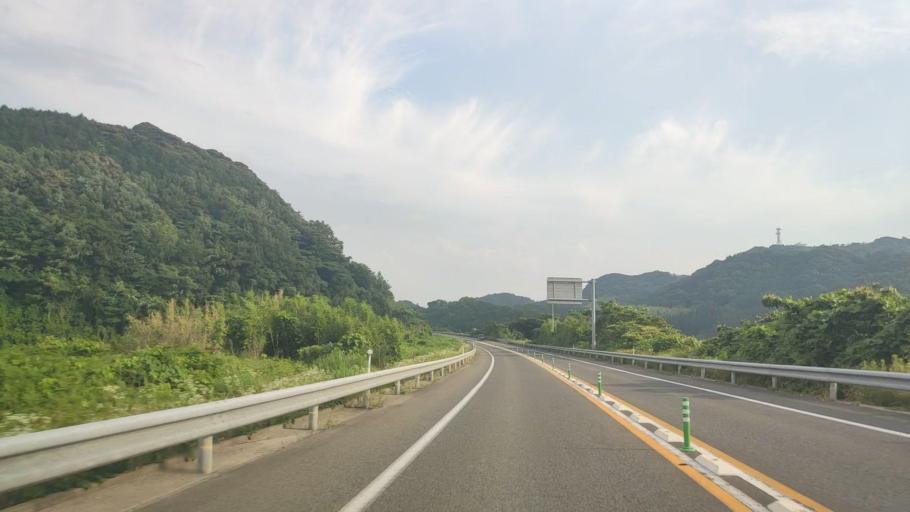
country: JP
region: Tottori
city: Kurayoshi
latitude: 35.4802
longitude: 133.8059
